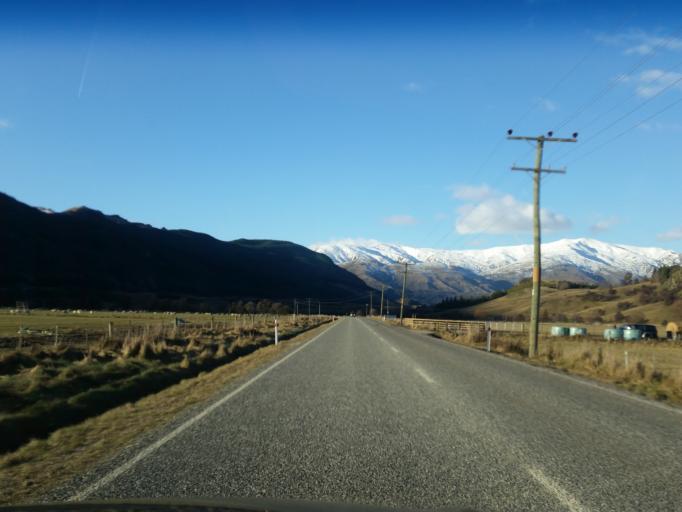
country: NZ
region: Otago
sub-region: Queenstown-Lakes District
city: Arrowtown
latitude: -44.9516
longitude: 168.7523
